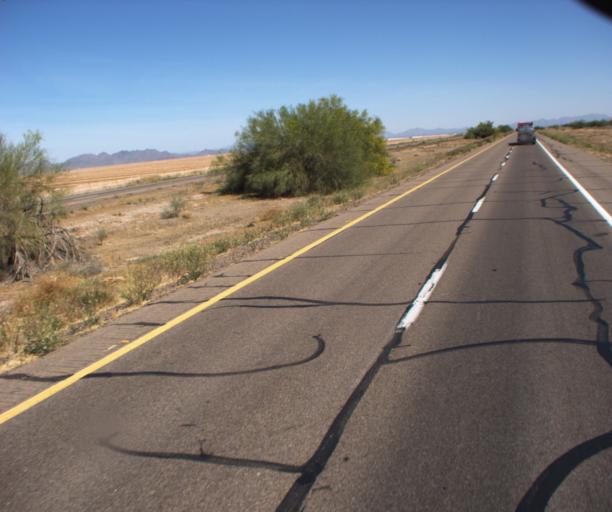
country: US
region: Arizona
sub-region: Maricopa County
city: Gila Bend
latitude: 32.9256
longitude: -112.8584
